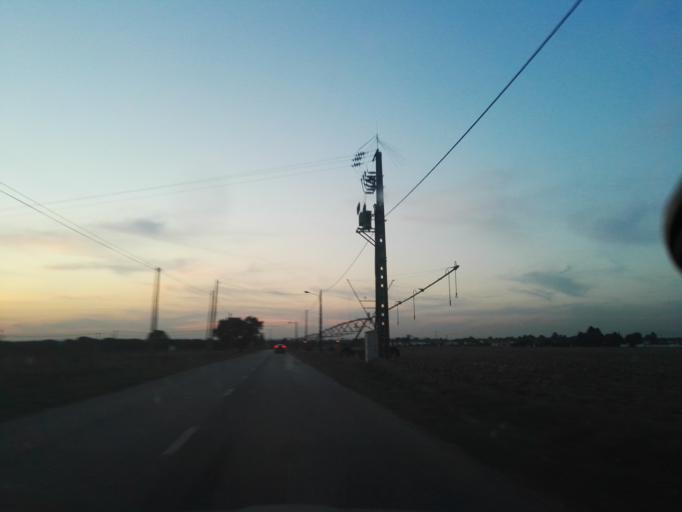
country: PT
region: Santarem
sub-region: Benavente
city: Benavente
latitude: 38.9468
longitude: -8.8143
